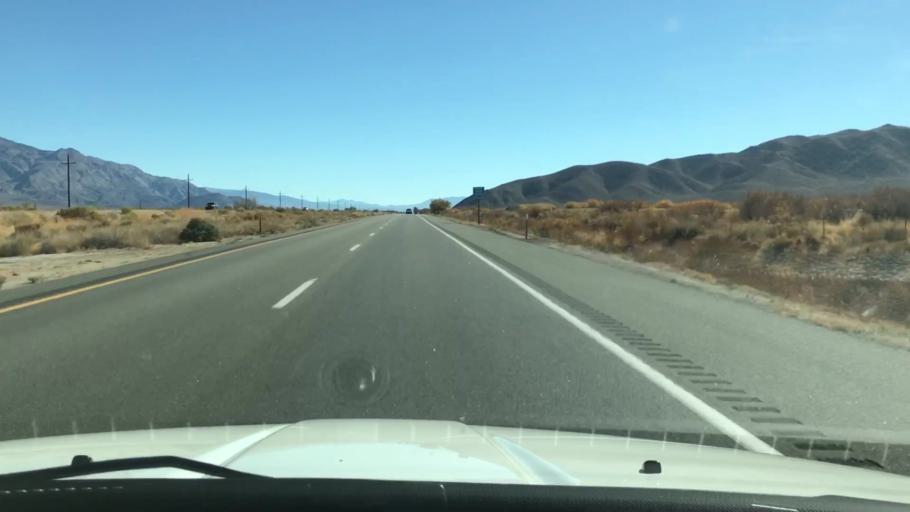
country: US
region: California
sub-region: Inyo County
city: Lone Pine
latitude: 36.7001
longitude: -118.1217
